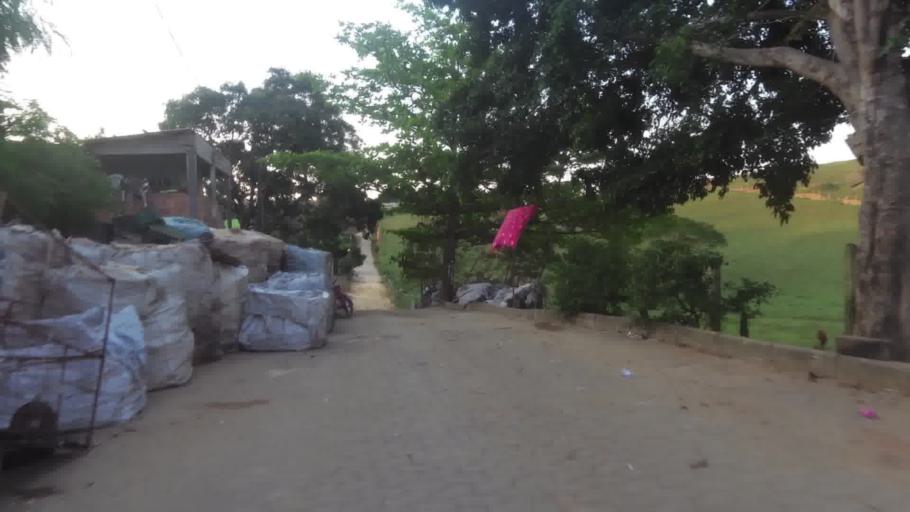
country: BR
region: Espirito Santo
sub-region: Piuma
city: Piuma
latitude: -20.8255
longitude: -40.7187
